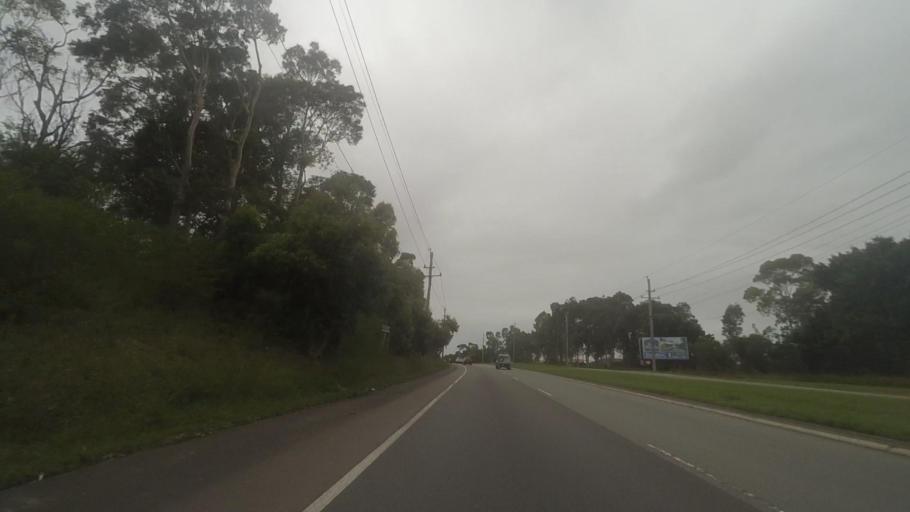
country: AU
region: New South Wales
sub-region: Newcastle
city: Mayfield West
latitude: -32.8775
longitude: 151.7146
